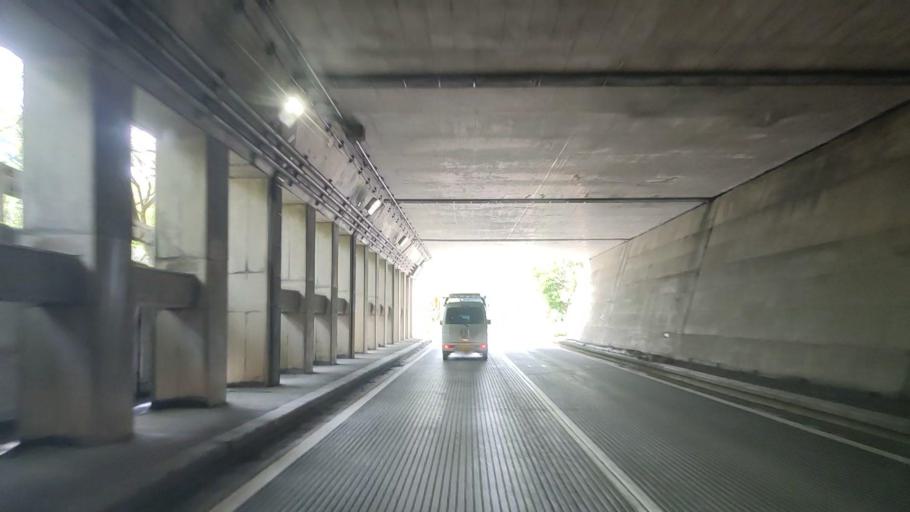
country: JP
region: Gifu
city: Takayama
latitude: 36.2567
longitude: 137.4718
